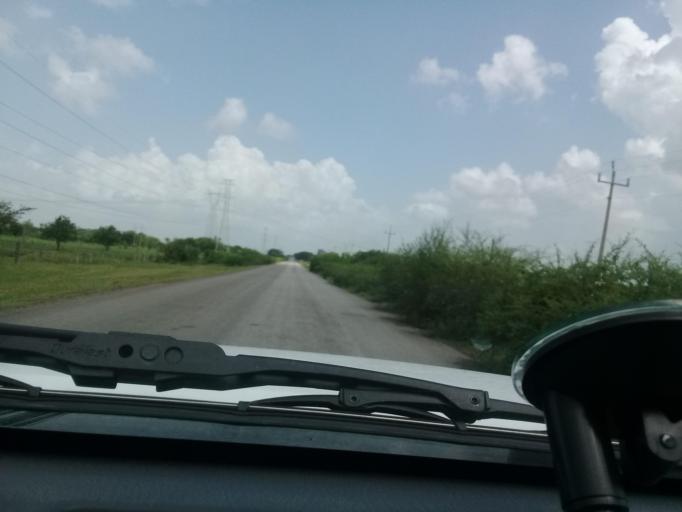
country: MX
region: Veracruz
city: Moralillo
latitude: 22.2224
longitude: -98.0072
